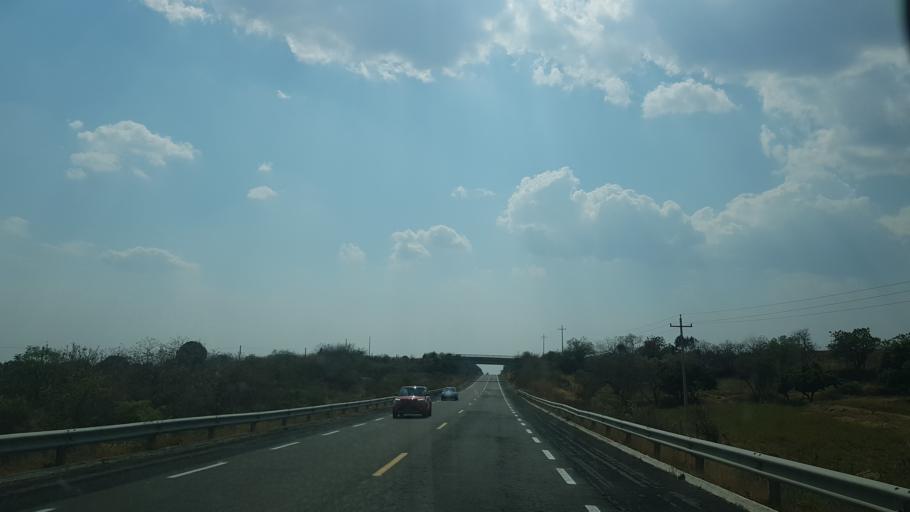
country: MX
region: Puebla
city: San Juan Amecac
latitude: 18.8165
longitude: -98.6609
